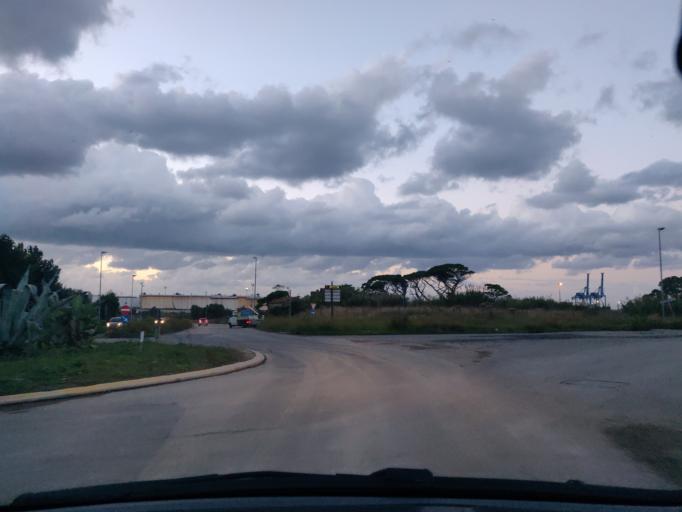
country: IT
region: Latium
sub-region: Citta metropolitana di Roma Capitale
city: Aurelia
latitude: 42.1164
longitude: 11.7787
